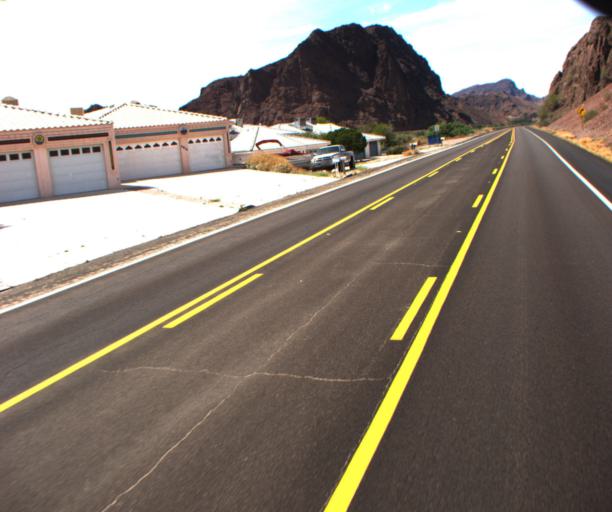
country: US
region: Arizona
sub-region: La Paz County
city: Cienega Springs
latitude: 34.2656
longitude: -114.1309
